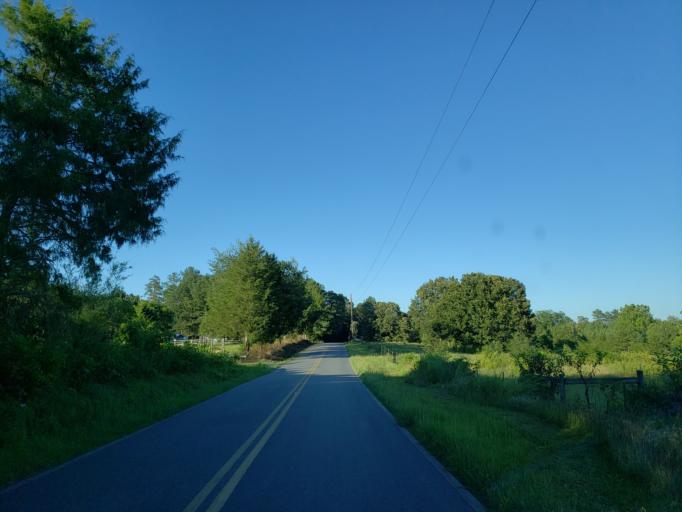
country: US
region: Georgia
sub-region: Polk County
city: Aragon
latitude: 34.0963
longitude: -85.0172
